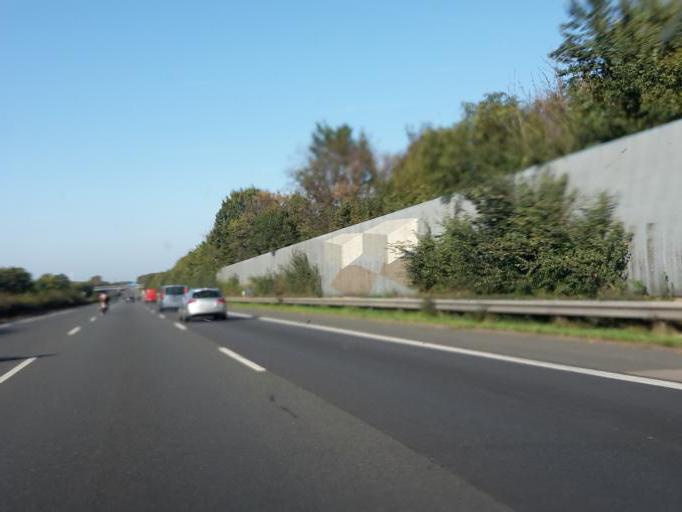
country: DE
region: North Rhine-Westphalia
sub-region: Regierungsbezirk Arnsberg
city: Unna
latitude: 51.5516
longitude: 7.6641
